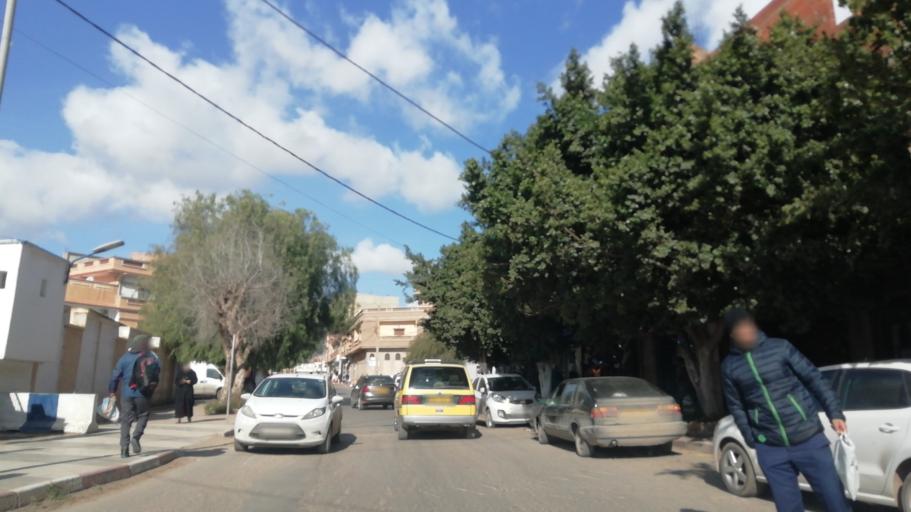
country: DZ
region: Oran
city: Es Senia
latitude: 35.6401
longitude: -0.6678
